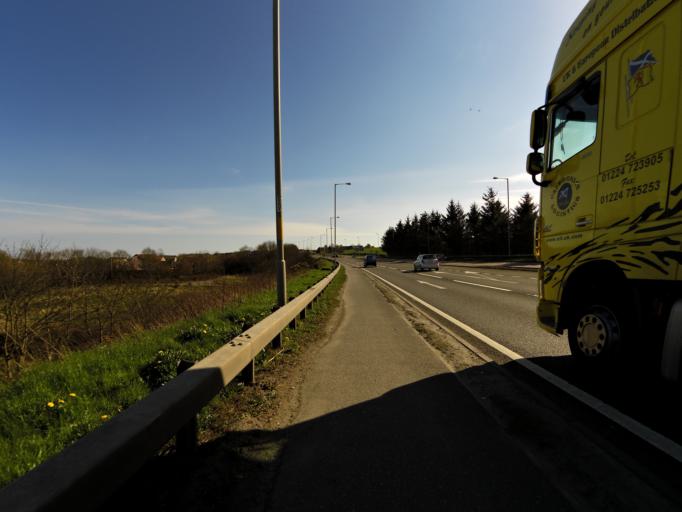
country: GB
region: Scotland
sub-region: Aberdeenshire
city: Newtonhill
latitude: 57.0411
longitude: -2.1534
